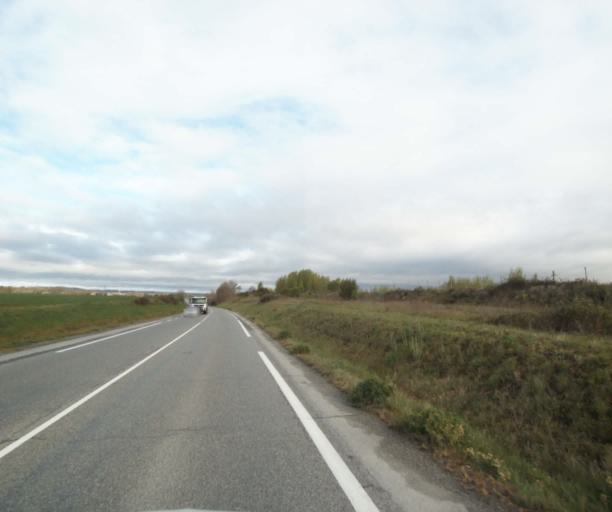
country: FR
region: Midi-Pyrenees
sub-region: Departement de l'Ariege
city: Saverdun
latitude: 43.2342
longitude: 1.5992
